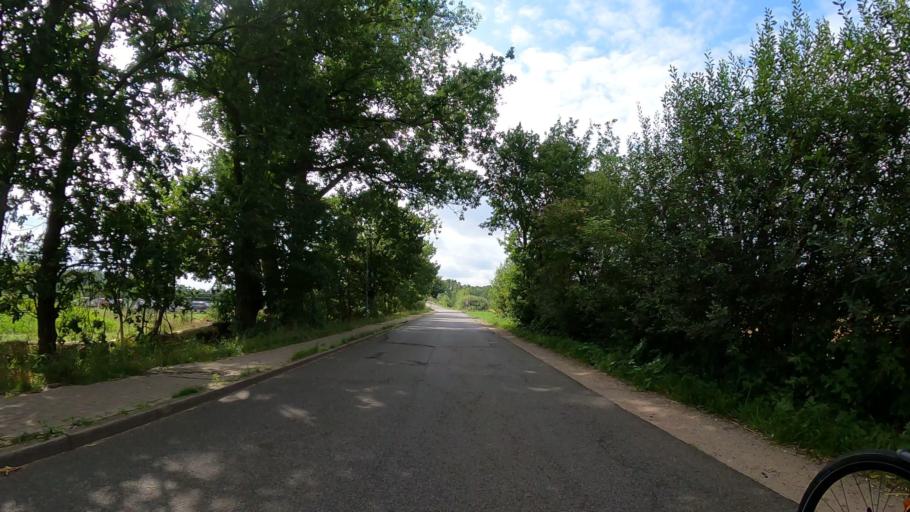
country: DE
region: Lower Saxony
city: Winsen
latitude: 53.3427
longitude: 10.2399
